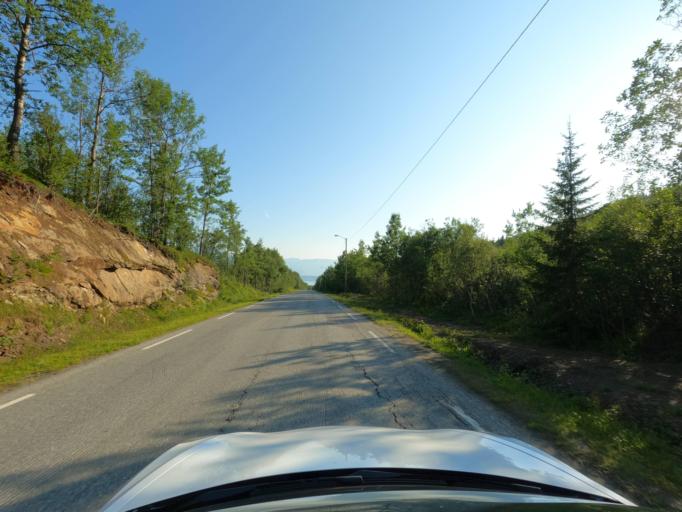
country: NO
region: Nordland
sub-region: Narvik
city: Bjerkvik
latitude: 68.5408
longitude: 17.4908
